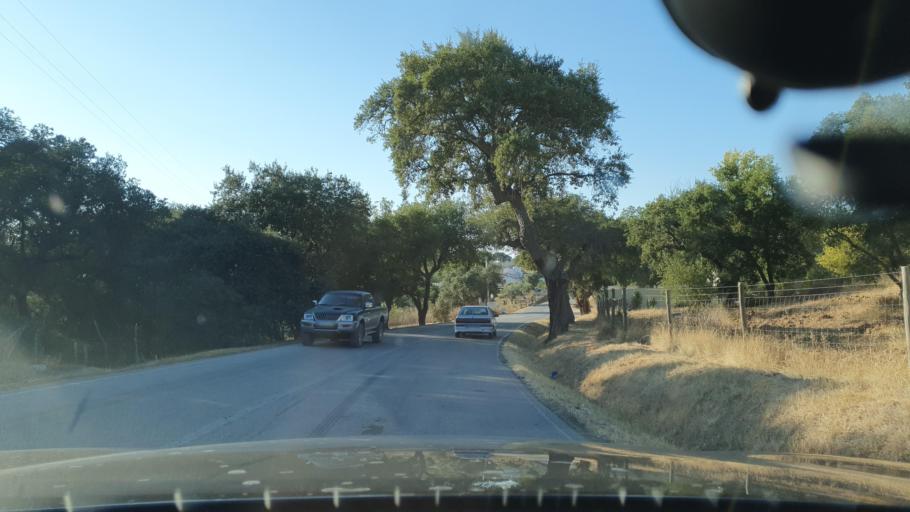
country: PT
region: Evora
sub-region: Estremoz
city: Estremoz
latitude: 38.8595
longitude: -7.6181
